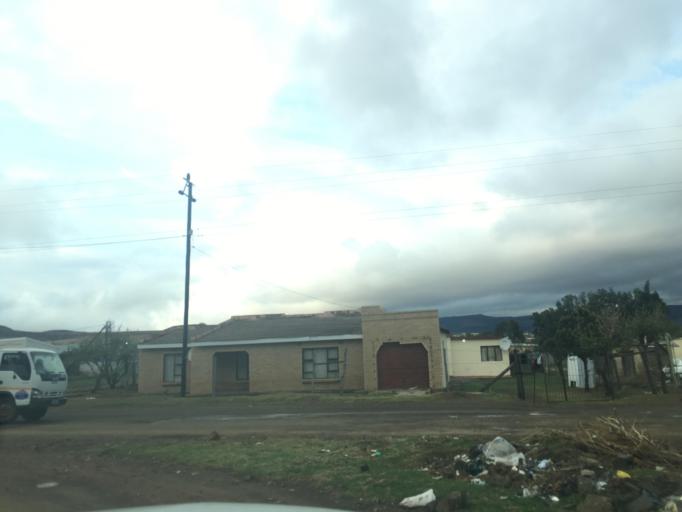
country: ZA
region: Eastern Cape
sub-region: Chris Hani District Municipality
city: Cala
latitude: -31.5290
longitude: 27.6978
